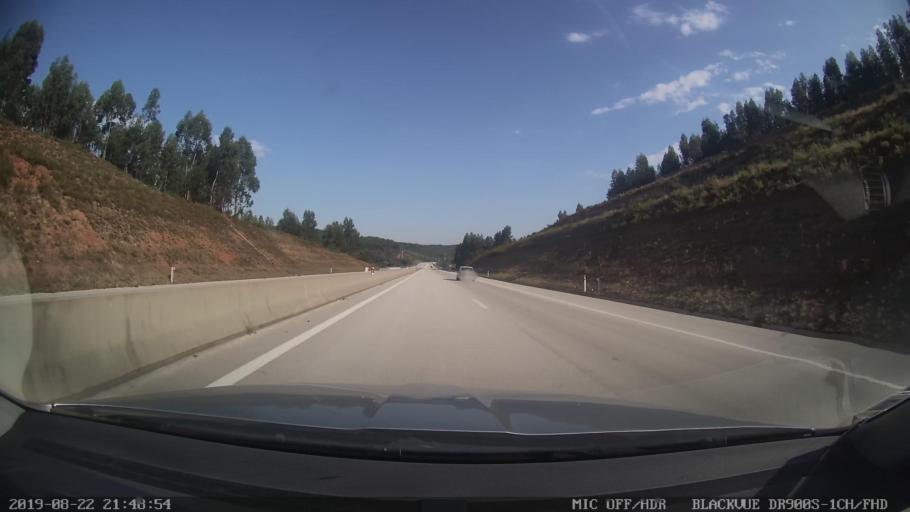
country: PT
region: Coimbra
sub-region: Penela
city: Penela
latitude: 40.0339
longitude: -8.3713
